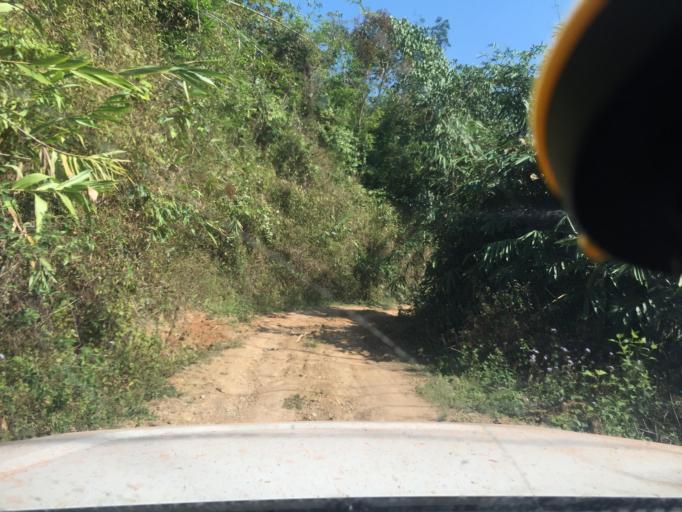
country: LA
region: Phongsali
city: Phongsali
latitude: 21.7040
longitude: 102.3909
